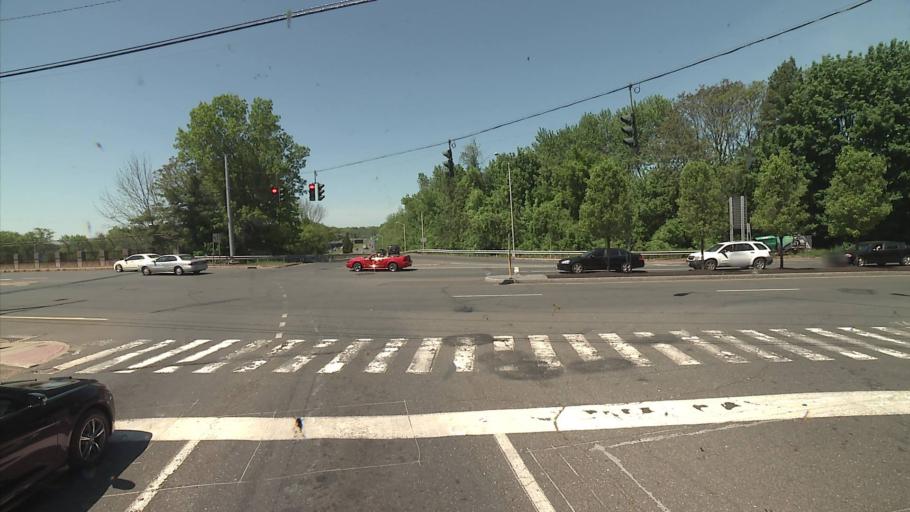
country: US
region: Connecticut
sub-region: Hartford County
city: West Hartford
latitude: 41.7359
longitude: -72.7427
